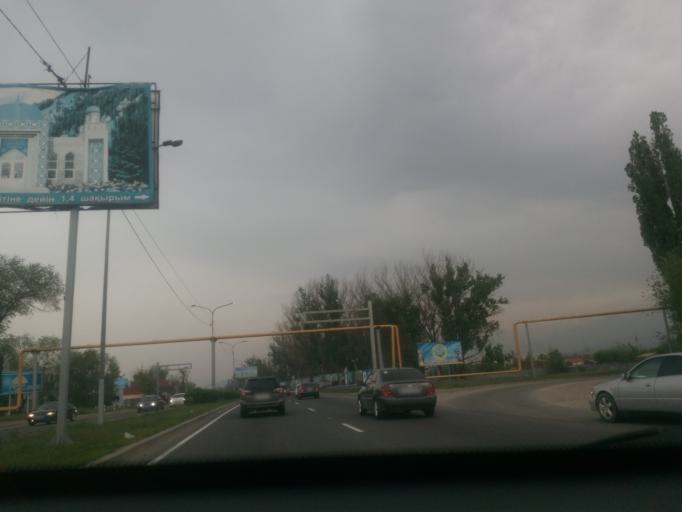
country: KZ
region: Almaty Oblysy
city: Burunday
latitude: 43.2288
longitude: 76.7614
